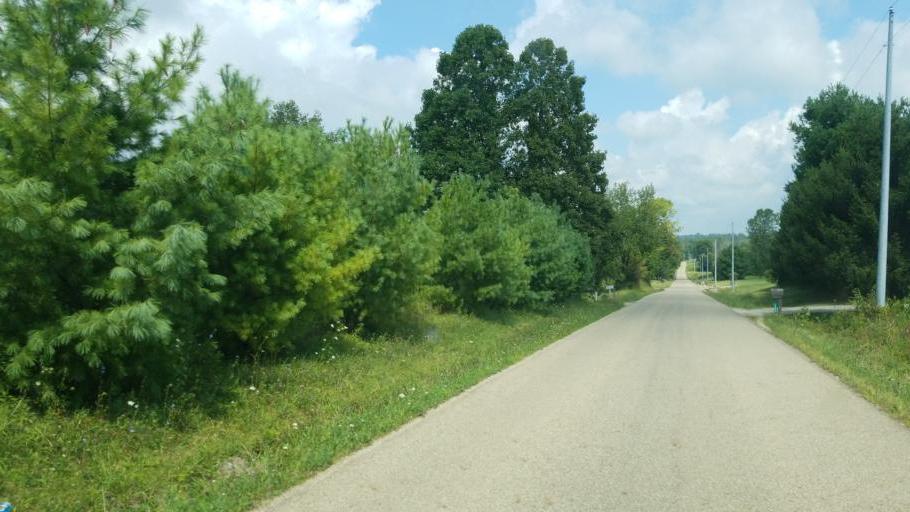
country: US
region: Ohio
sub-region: Licking County
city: Utica
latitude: 40.2562
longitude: -82.4361
